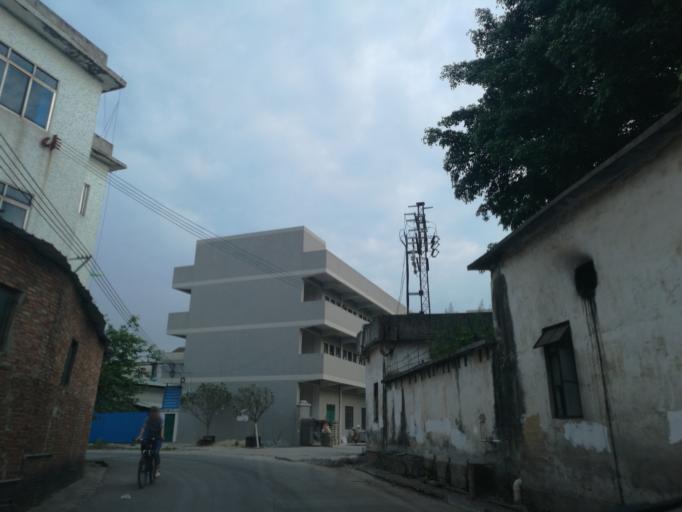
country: CN
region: Guangdong
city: Hengli
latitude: 23.0447
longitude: 113.9607
